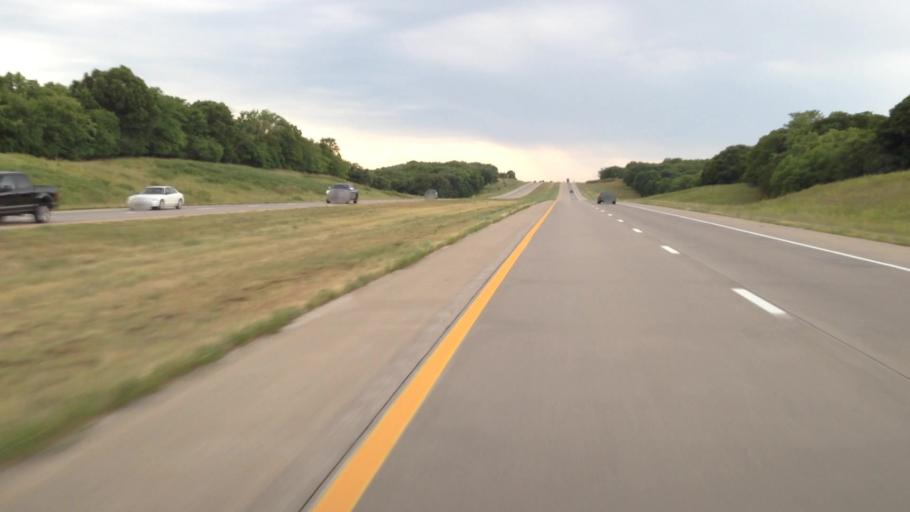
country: US
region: Kansas
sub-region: Osage County
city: Lyndon
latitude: 38.4822
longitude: -95.4969
